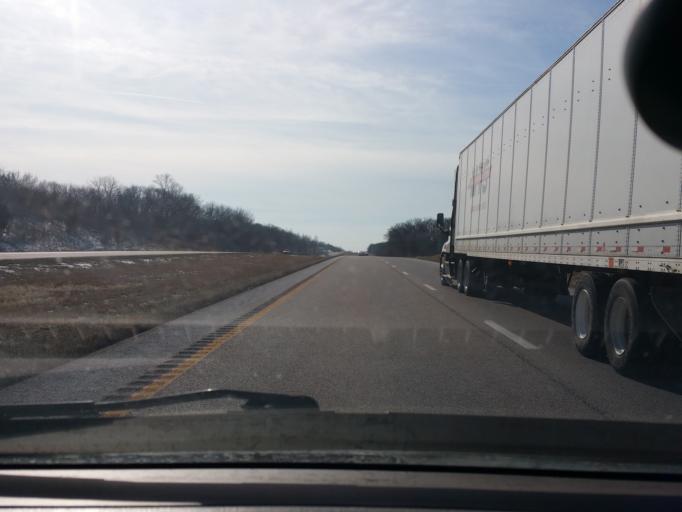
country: US
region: Missouri
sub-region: Clinton County
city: Lathrop
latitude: 39.4831
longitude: -94.3063
